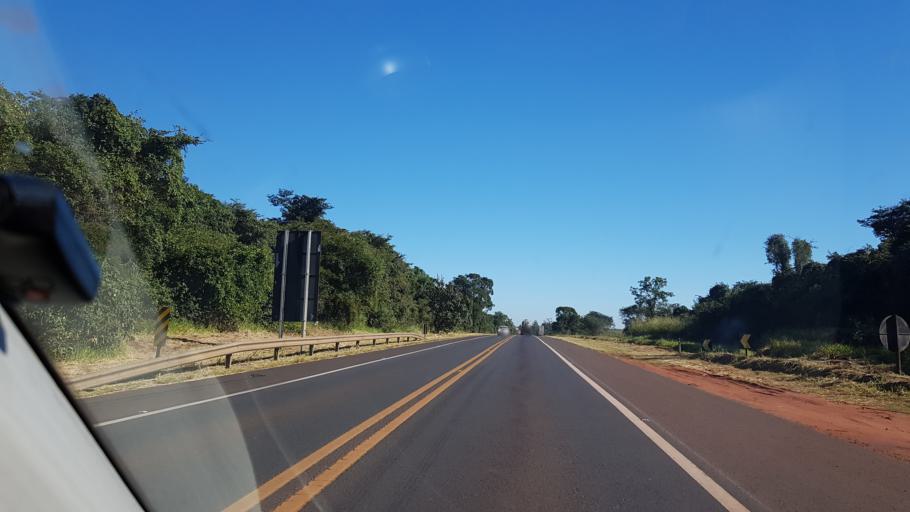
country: BR
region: Sao Paulo
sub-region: Assis
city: Assis
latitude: -22.5856
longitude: -50.4998
